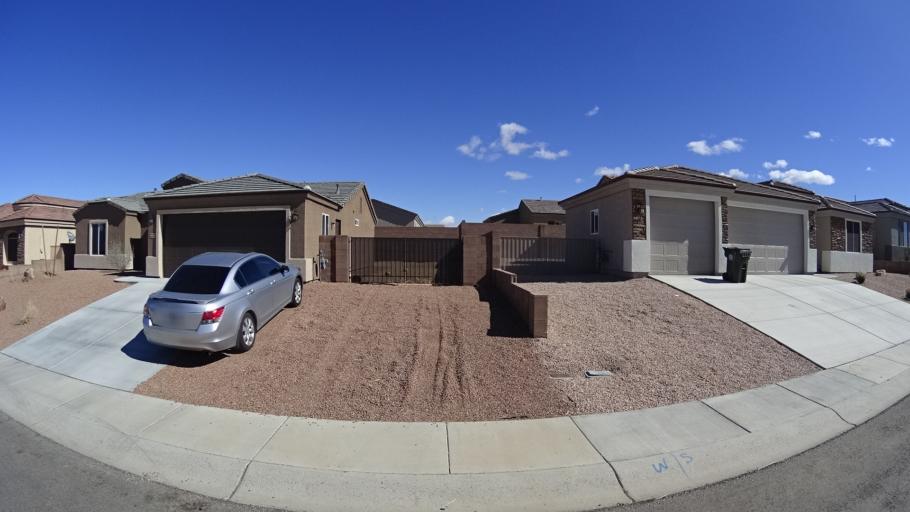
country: US
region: Arizona
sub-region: Mohave County
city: Kingman
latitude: 35.1893
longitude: -114.0067
